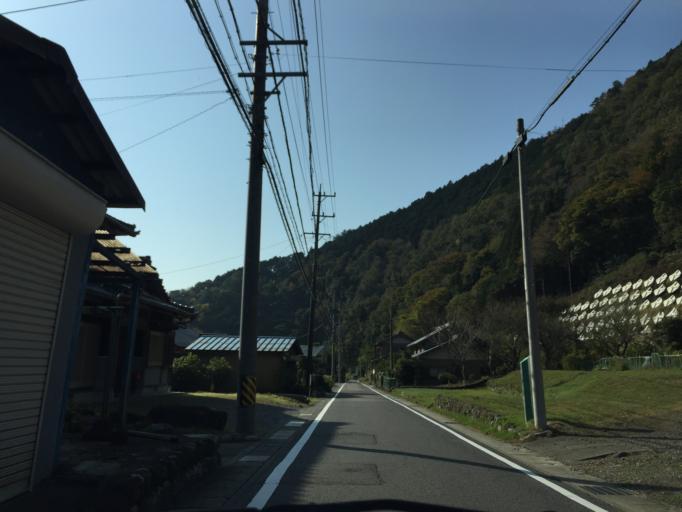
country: JP
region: Gifu
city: Minokamo
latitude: 35.5486
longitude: 137.1195
